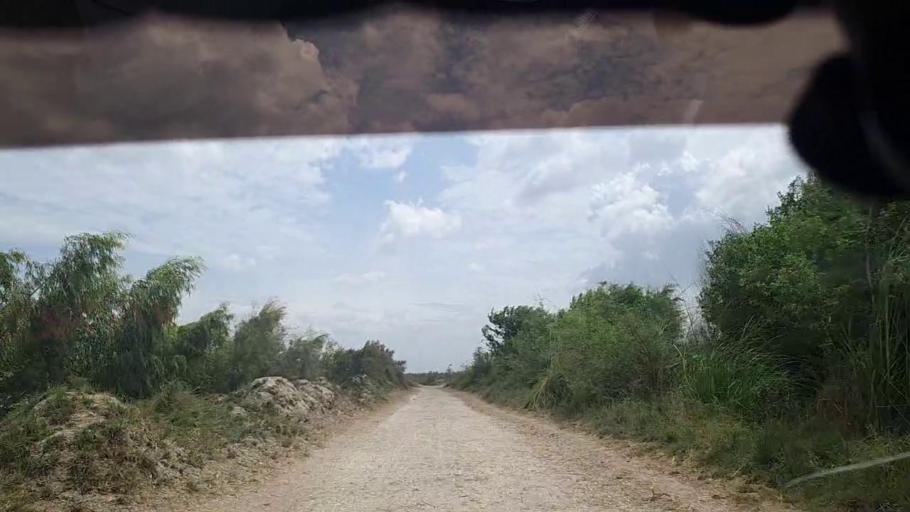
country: PK
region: Sindh
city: Rustam jo Goth
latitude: 28.0458
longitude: 68.9418
